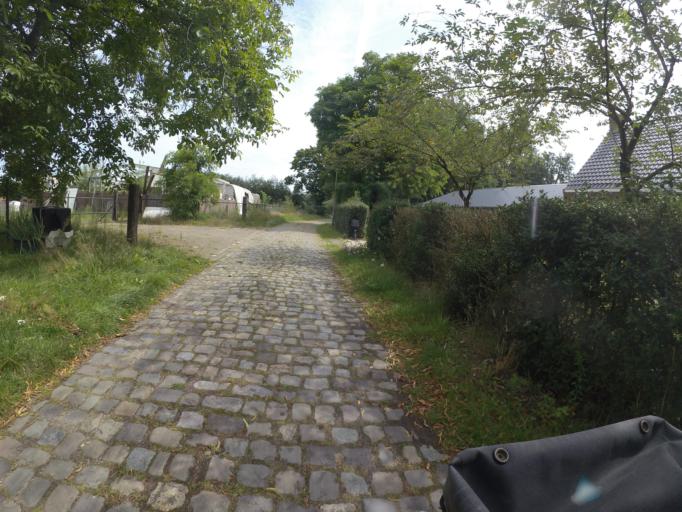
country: NL
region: North Brabant
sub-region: Gemeente Valkenswaard
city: Valkenswaard
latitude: 51.2982
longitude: 5.4286
